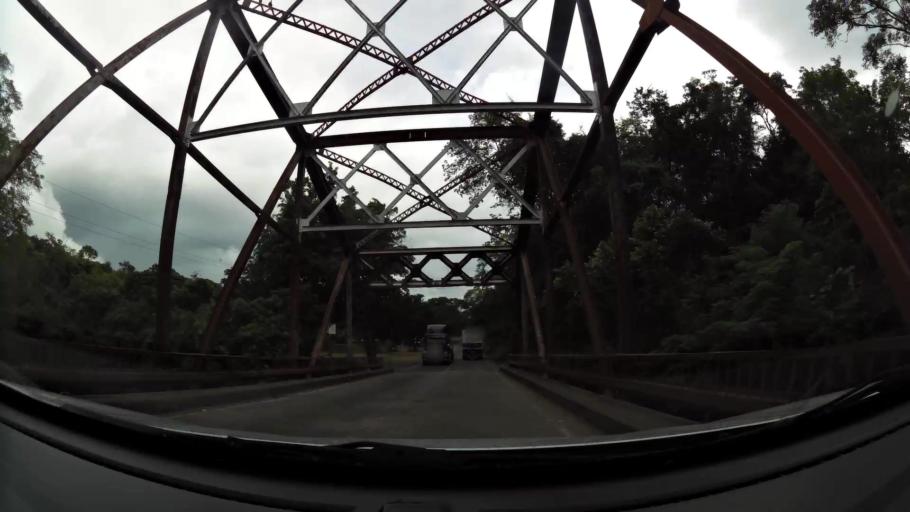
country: CR
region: Guanacaste
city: Juntas
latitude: 10.2520
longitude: -85.0543
